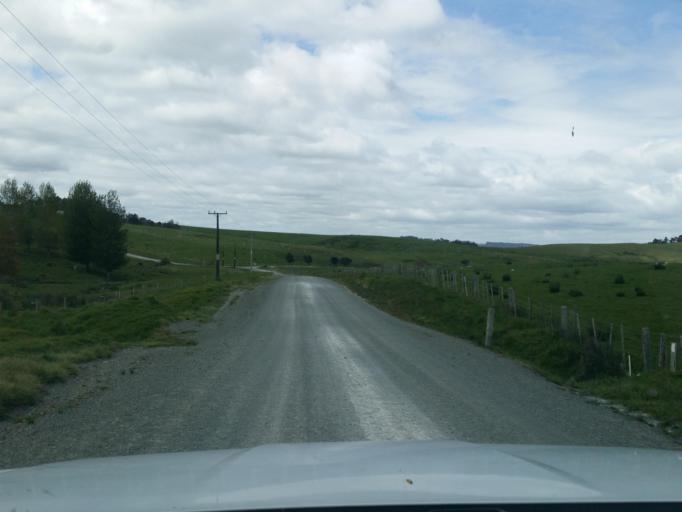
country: NZ
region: Auckland
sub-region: Auckland
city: Wellsford
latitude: -36.2875
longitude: 174.3295
